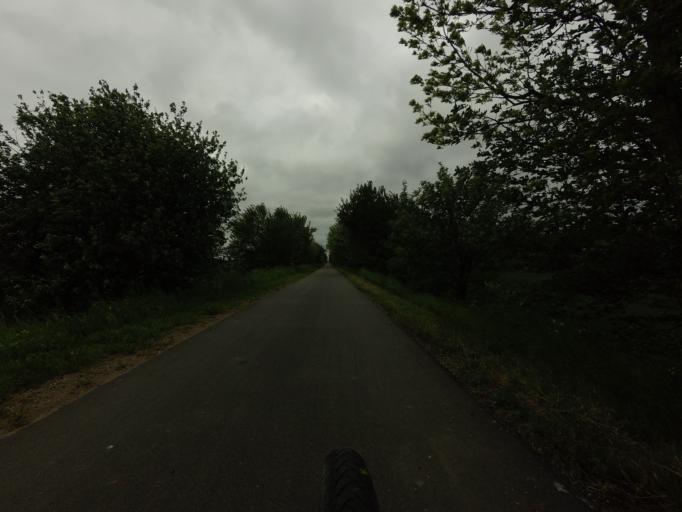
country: DK
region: Zealand
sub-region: Slagelse Kommune
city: Skaelskor
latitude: 55.2613
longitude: 11.3918
